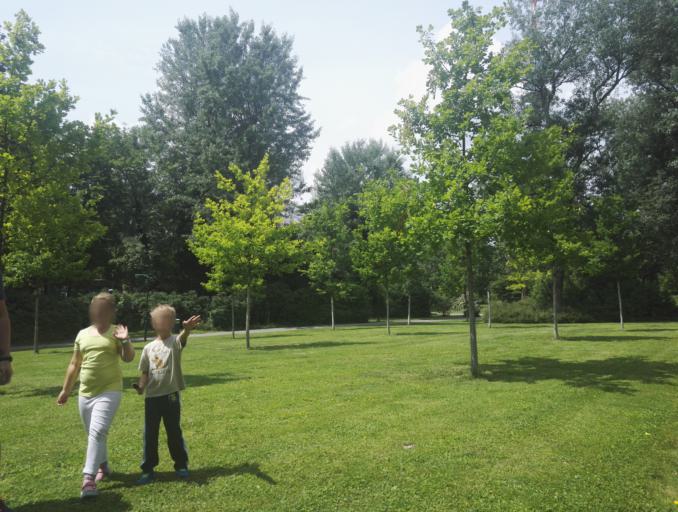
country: AT
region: Vienna
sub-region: Wien Stadt
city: Vienna
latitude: 48.2409
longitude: 16.4162
